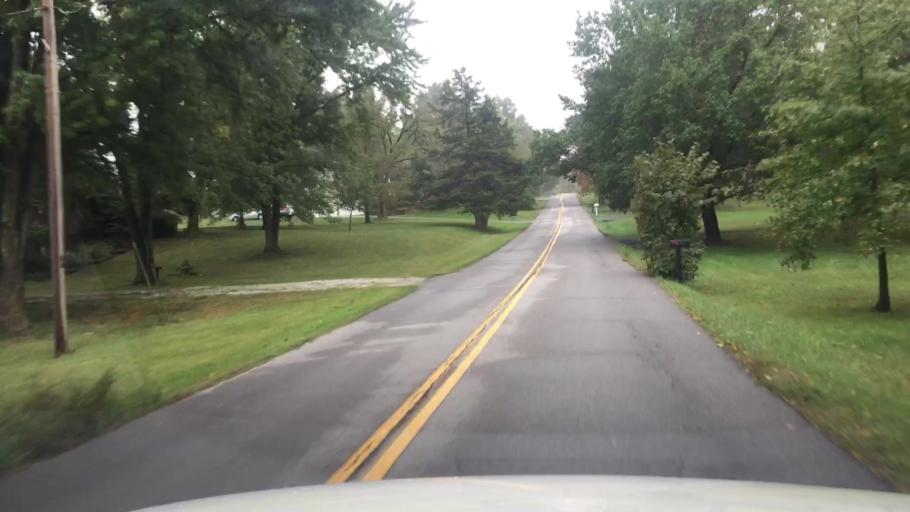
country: US
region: Missouri
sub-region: Boone County
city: Columbia
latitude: 38.8598
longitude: -92.3149
